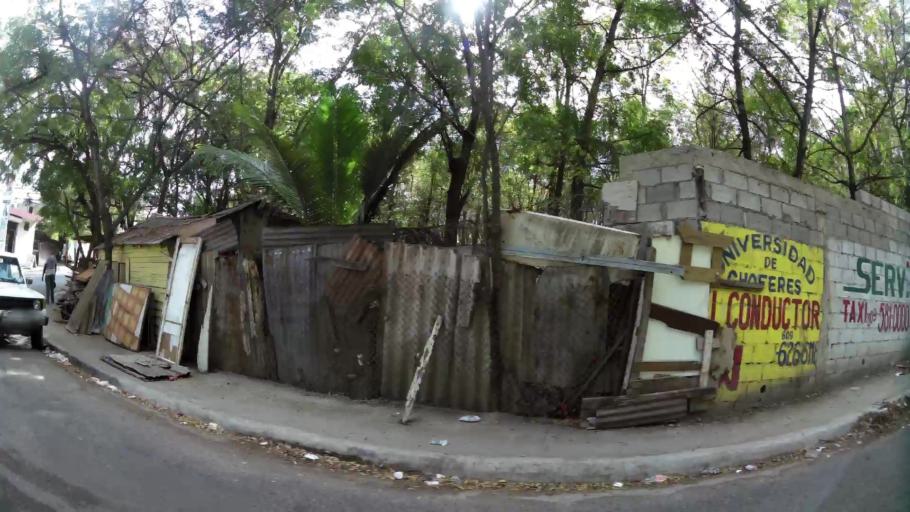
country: DO
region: Santiago
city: Santiago de los Caballeros
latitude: 19.4275
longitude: -70.6833
